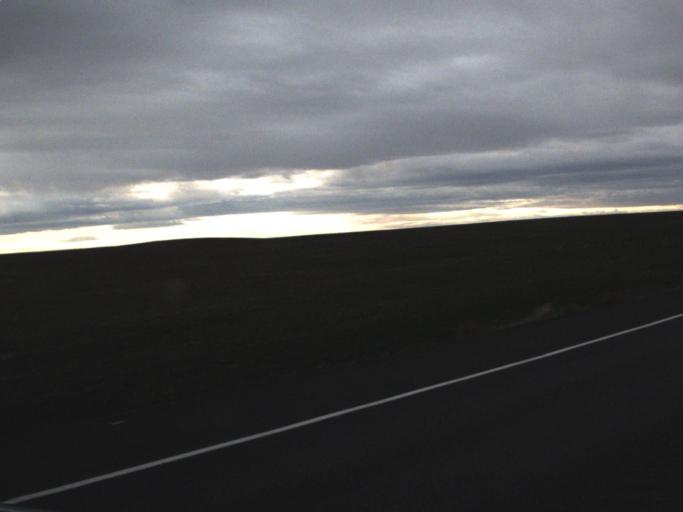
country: US
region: Washington
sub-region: Adams County
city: Ritzville
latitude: 46.7952
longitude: -118.4054
